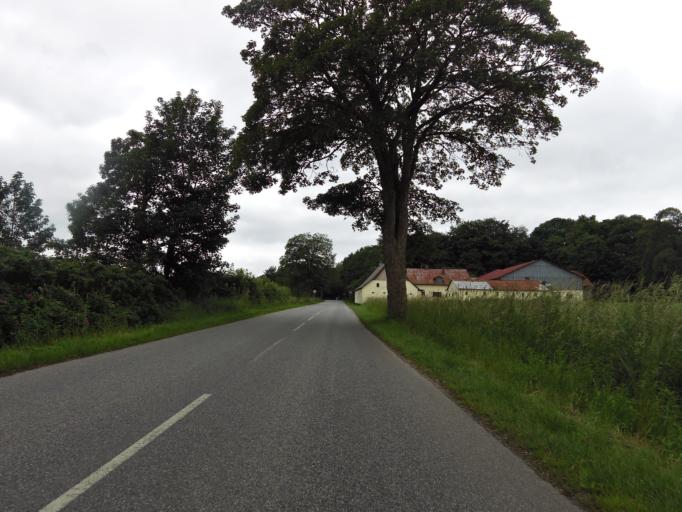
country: DK
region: South Denmark
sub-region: Tonder Kommune
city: Toftlund
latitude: 55.1019
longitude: 9.1072
